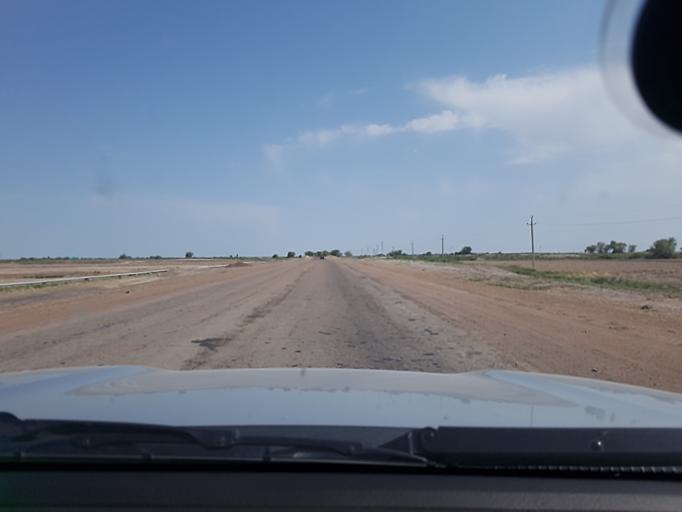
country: TM
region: Dasoguz
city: Boldumsaz
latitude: 42.1966
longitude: 59.5425
